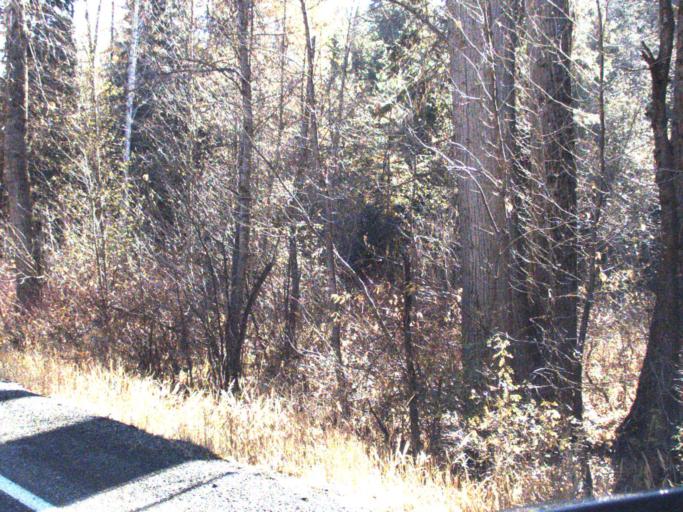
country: US
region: Washington
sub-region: Ferry County
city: Republic
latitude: 48.5978
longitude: -118.6478
